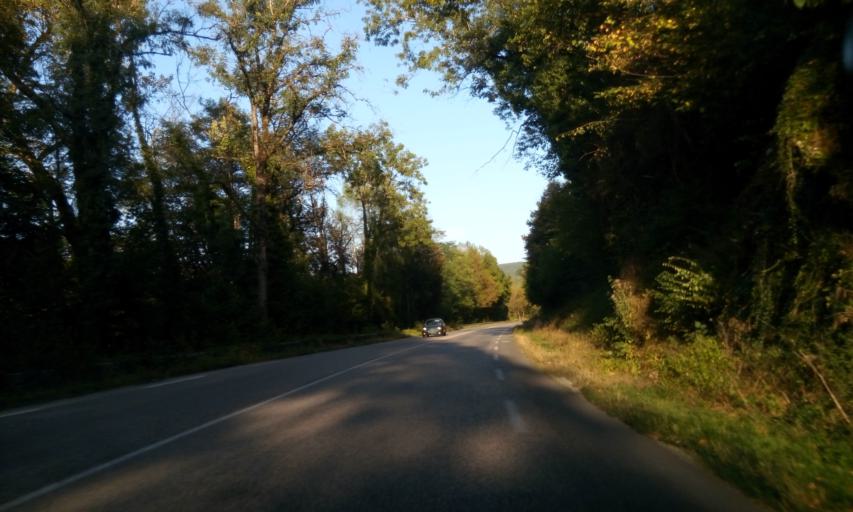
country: FR
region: Rhone-Alpes
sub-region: Departement de l'Ain
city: Poncin
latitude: 46.0841
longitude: 5.3940
